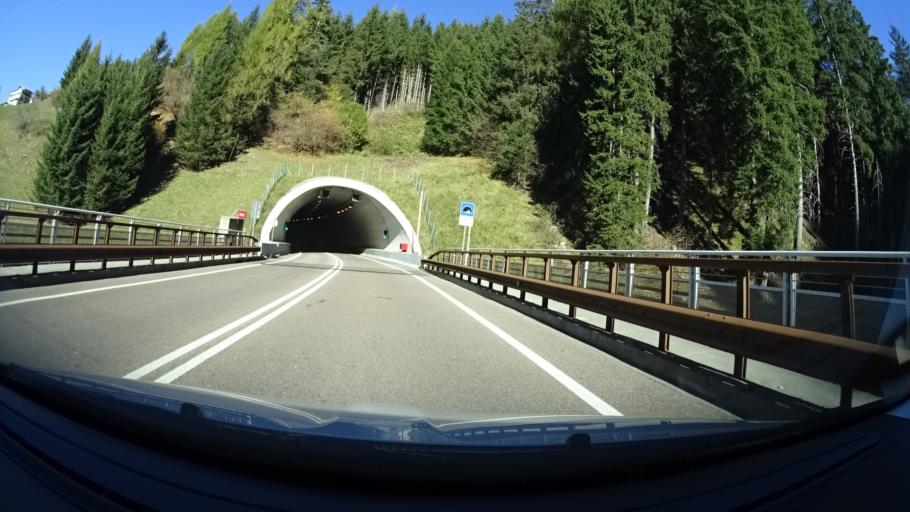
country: IT
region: Trentino-Alto Adige
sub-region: Provincia di Trento
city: Moena
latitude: 46.3748
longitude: 11.6705
